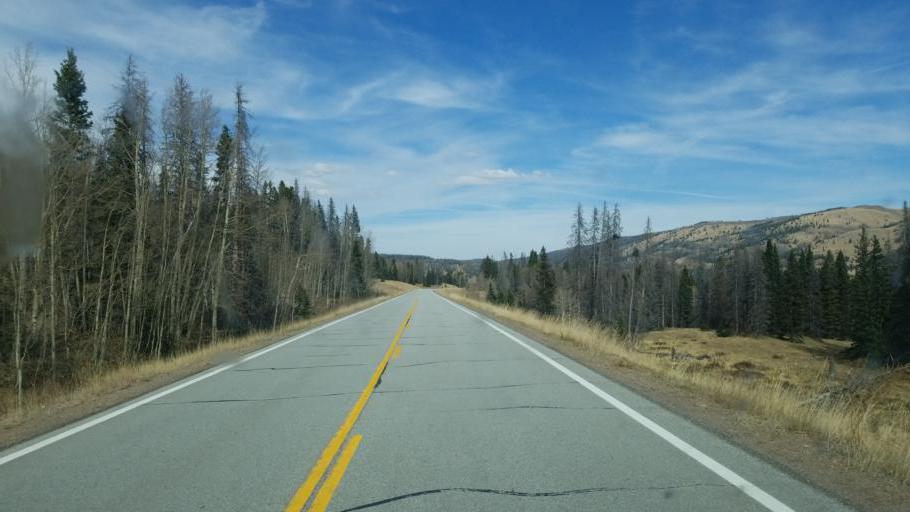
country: US
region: New Mexico
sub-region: Rio Arriba County
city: Chama
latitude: 37.0188
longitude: -106.4163
